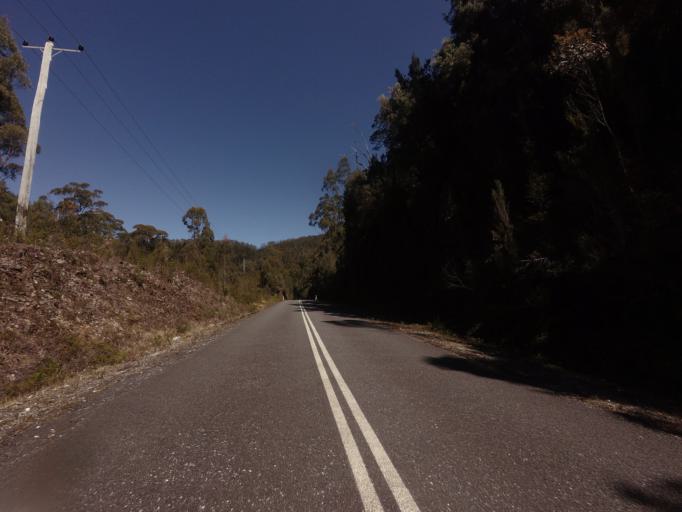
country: AU
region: Tasmania
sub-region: West Coast
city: Queenstown
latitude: -42.7647
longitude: 146.0055
